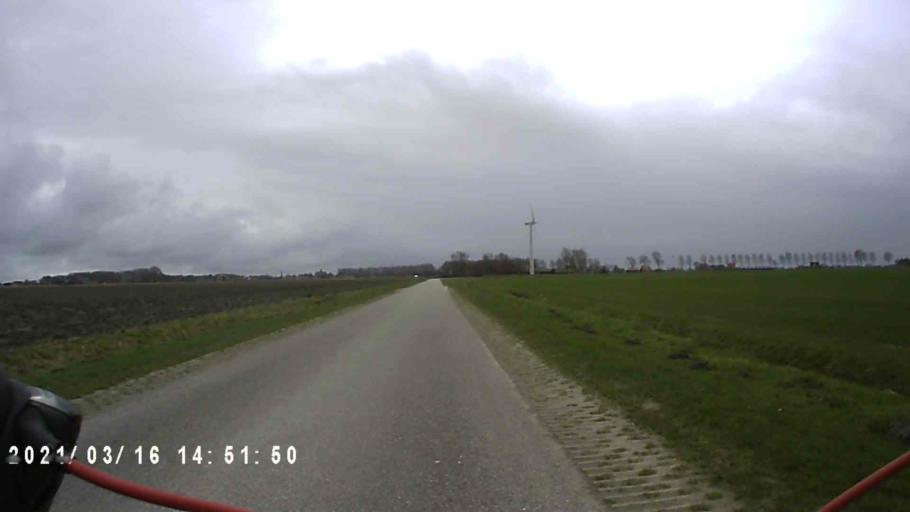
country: NL
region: Friesland
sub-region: Gemeente Harlingen
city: Harlingen
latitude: 53.1149
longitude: 5.4640
